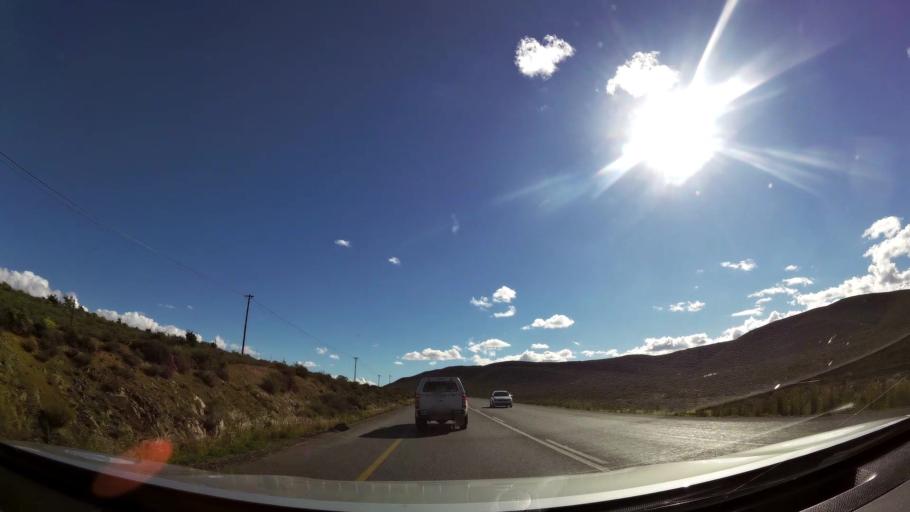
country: ZA
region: Western Cape
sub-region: Cape Winelands District Municipality
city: Worcester
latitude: -33.7358
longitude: 19.6742
